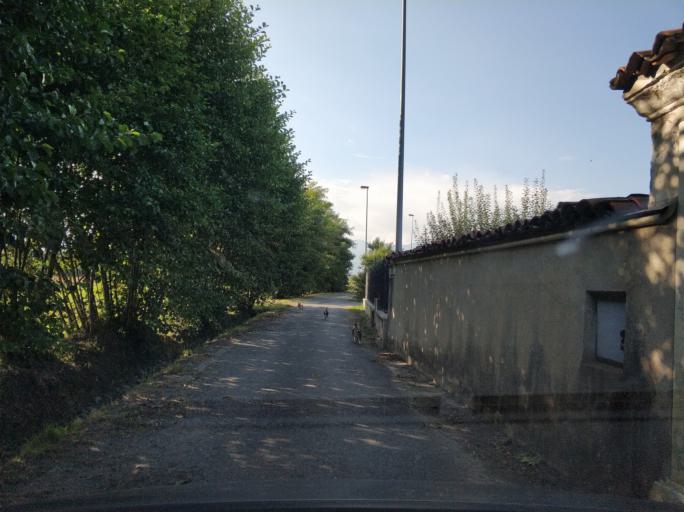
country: IT
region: Piedmont
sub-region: Provincia di Torino
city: San Maurizio
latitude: 45.2033
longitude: 7.6124
